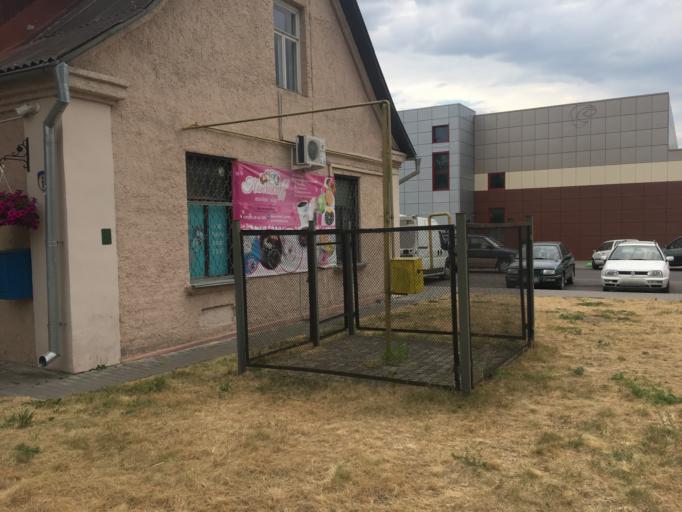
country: BY
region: Grodnenskaya
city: Hrodna
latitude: 53.6894
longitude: 23.8446
